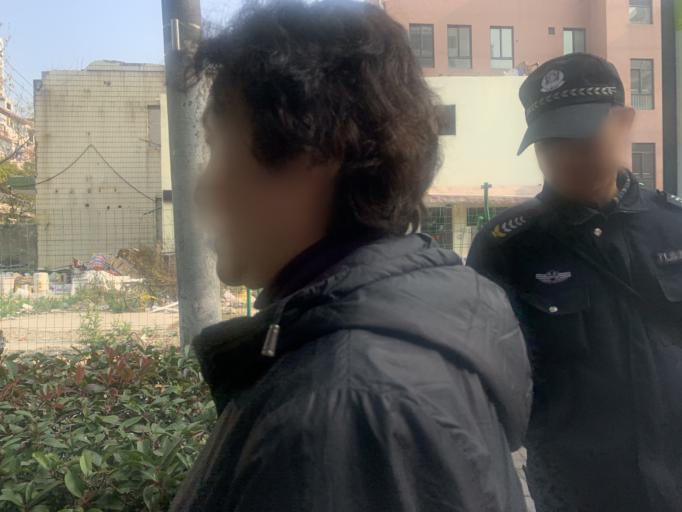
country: CN
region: Shanghai Shi
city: Huamu
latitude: 31.1845
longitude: 121.5150
